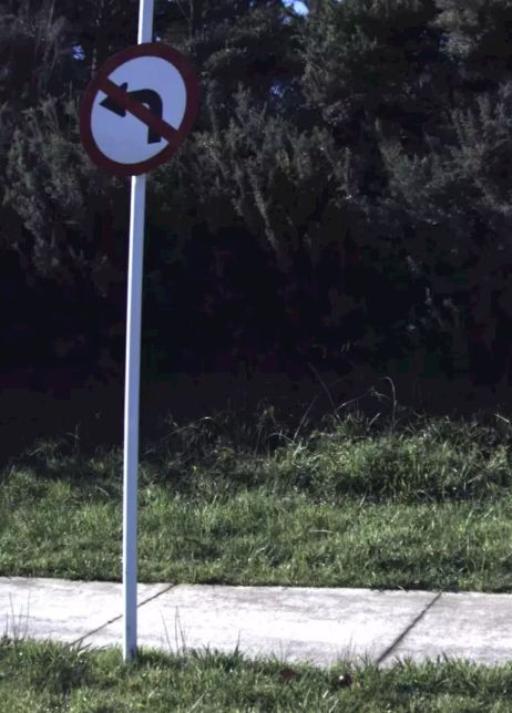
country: NZ
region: Auckland
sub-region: Auckland
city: Rothesay Bay
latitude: -36.6051
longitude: 174.6716
